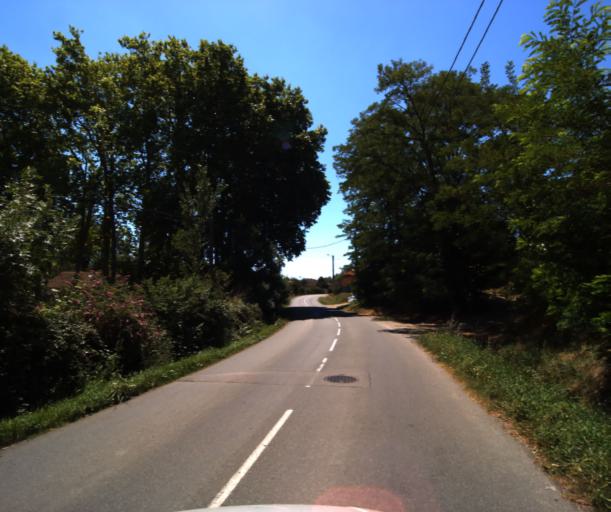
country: FR
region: Midi-Pyrenees
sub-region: Departement de la Haute-Garonne
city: Muret
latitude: 43.4609
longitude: 1.3163
